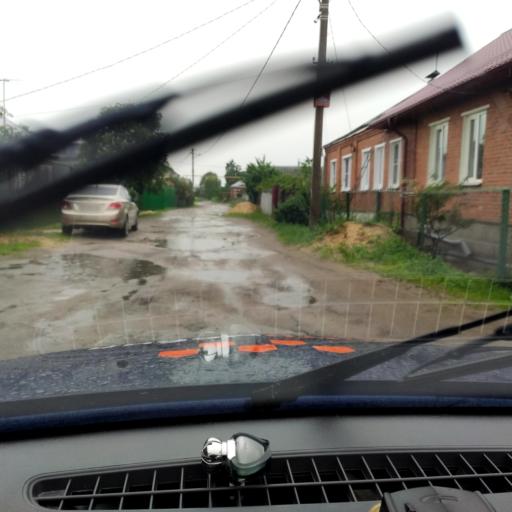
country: RU
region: Voronezj
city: Somovo
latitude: 51.7462
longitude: 39.3370
